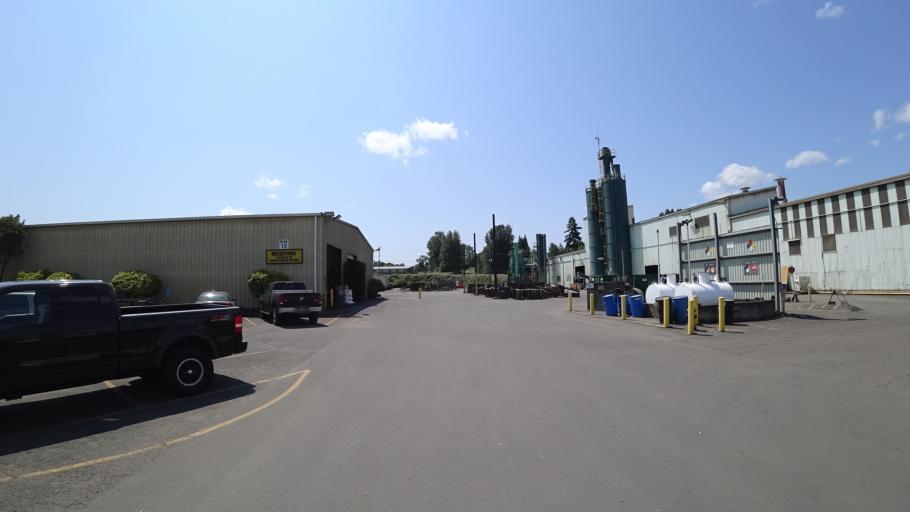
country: US
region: Washington
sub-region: Clark County
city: Vancouver
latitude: 45.5991
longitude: -122.7281
